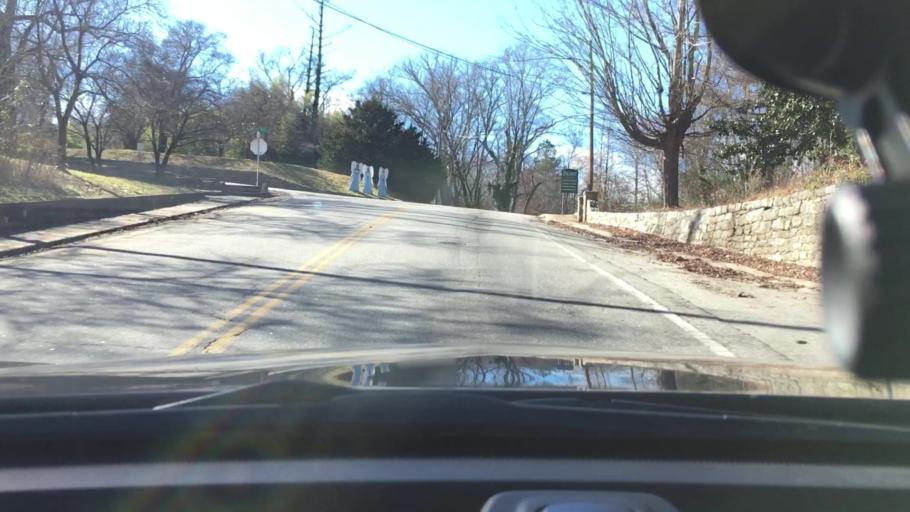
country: US
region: South Carolina
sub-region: Spartanburg County
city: Pacolet
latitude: 34.9197
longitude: -81.7453
